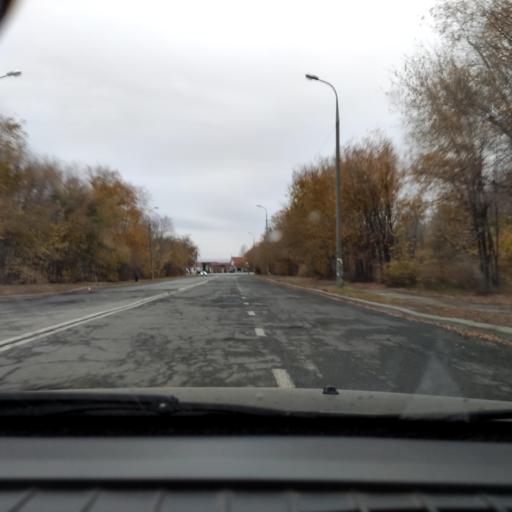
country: RU
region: Samara
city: Tol'yatti
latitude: 53.5039
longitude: 49.2526
